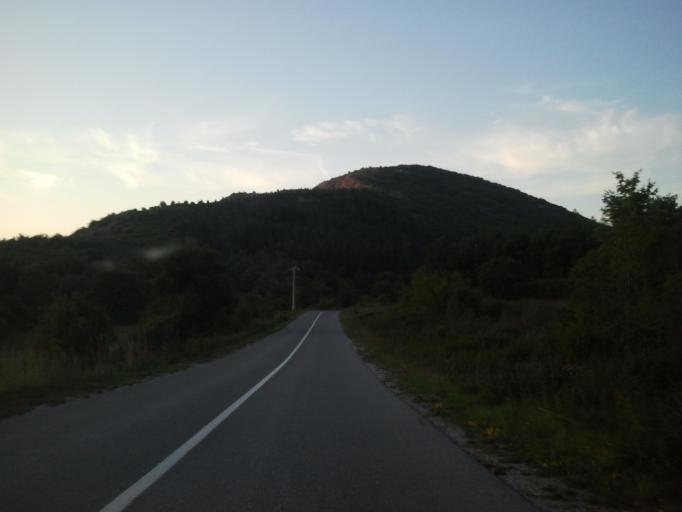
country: HR
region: Zadarska
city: Obrovac
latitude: 44.4261
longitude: 15.6602
